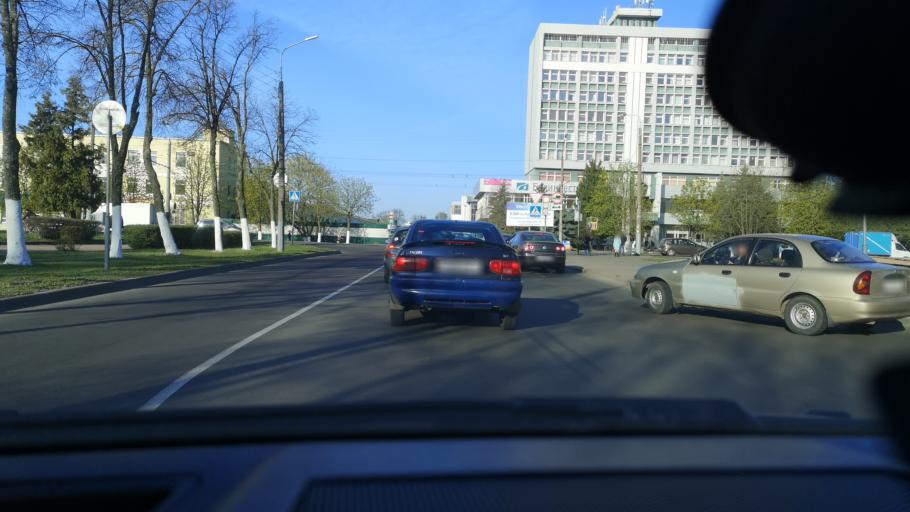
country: BY
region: Gomel
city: Gomel
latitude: 52.4502
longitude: 30.9971
